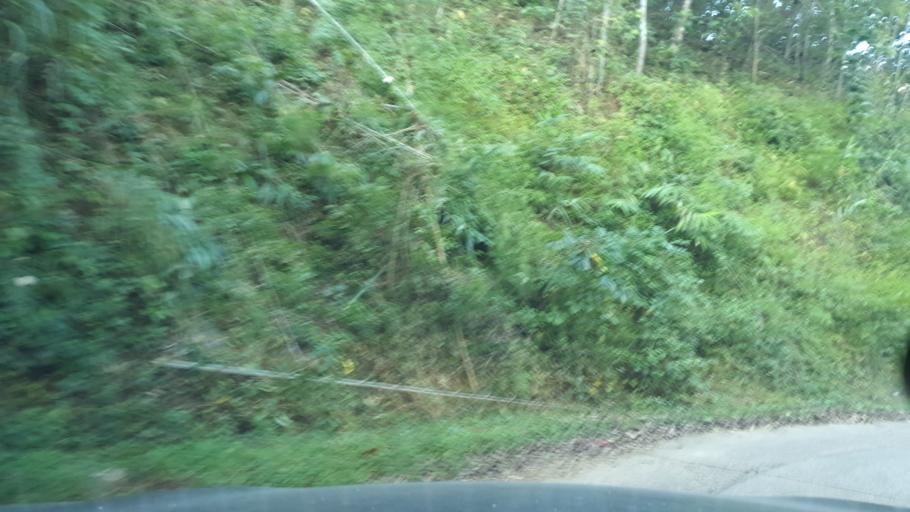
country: TH
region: Chiang Mai
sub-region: Amphoe Chiang Dao
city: Chiang Dao
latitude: 19.3857
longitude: 98.7703
